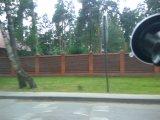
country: RU
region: Moskovskaya
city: Zhukovskiy
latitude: 55.5852
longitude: 38.1486
